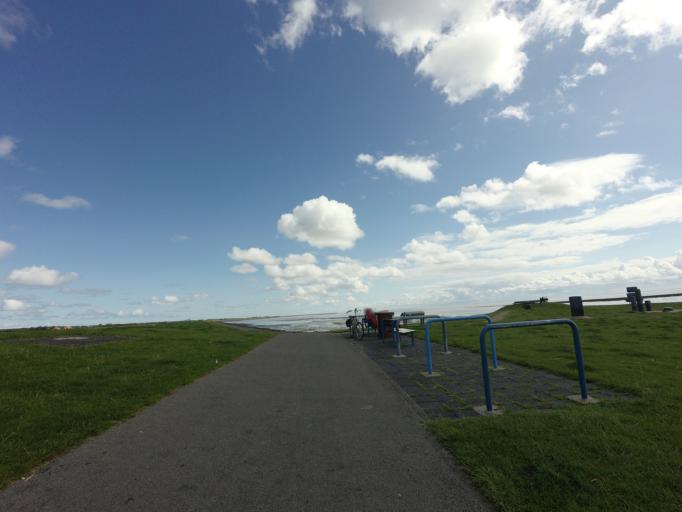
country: NL
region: Friesland
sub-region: Gemeente Terschelling
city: West-Terschelling
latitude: 53.3660
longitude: 5.2425
